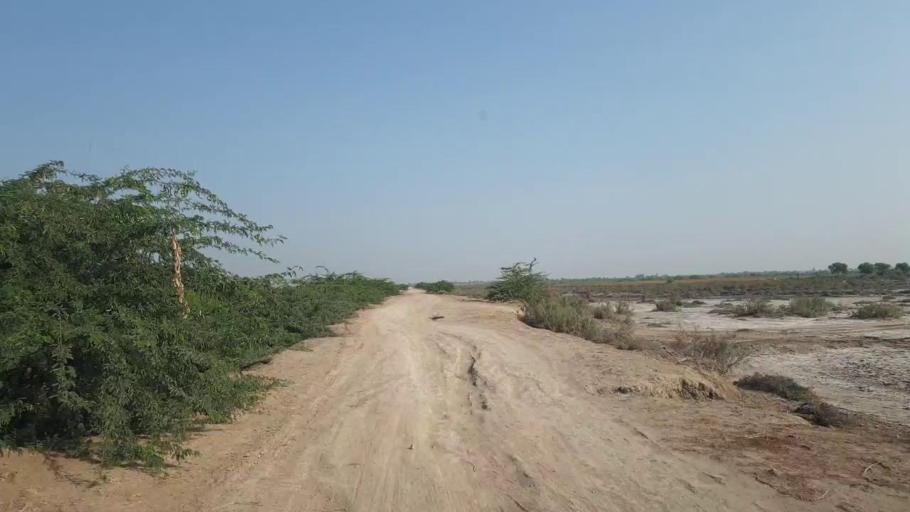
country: PK
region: Sindh
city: Badin
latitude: 24.4751
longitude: 68.7426
